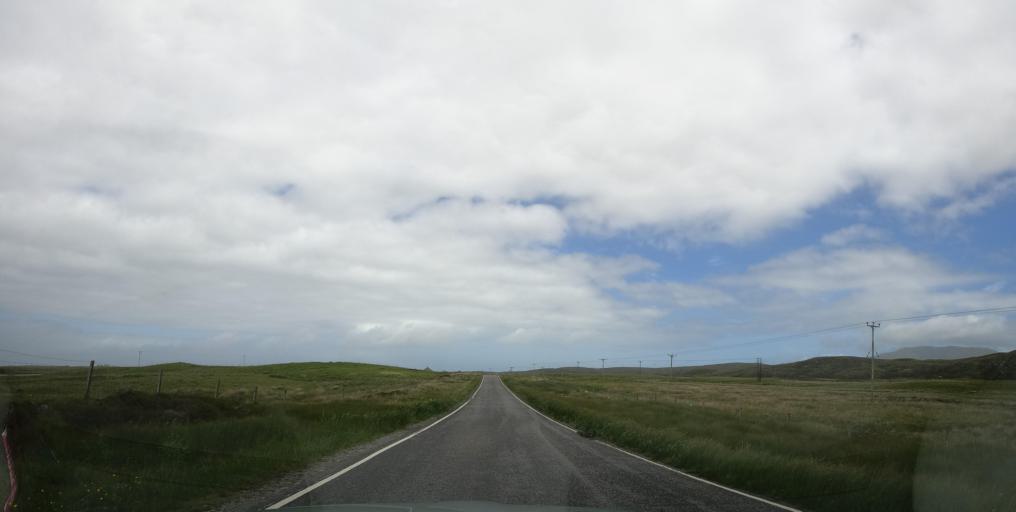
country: GB
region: Scotland
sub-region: Eilean Siar
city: Isle of South Uist
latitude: 57.2127
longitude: -7.3945
